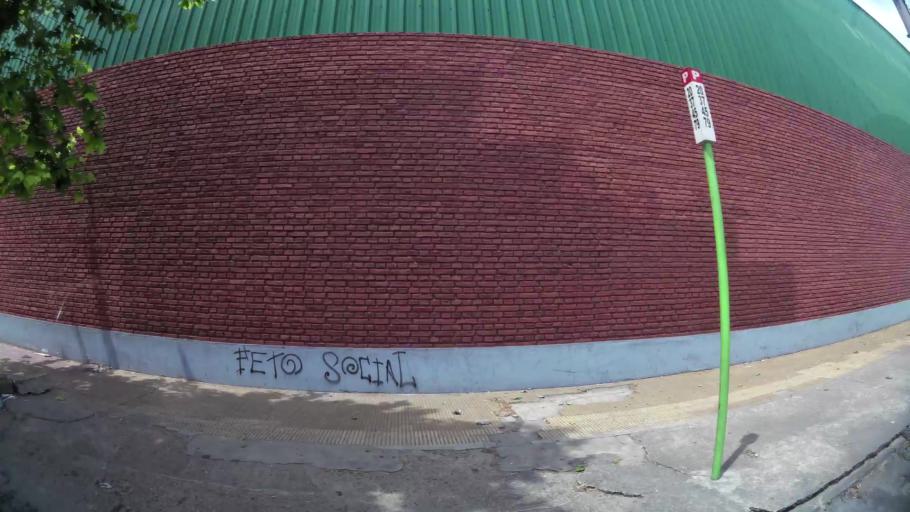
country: AR
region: Buenos Aires
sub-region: Partido de Avellaneda
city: Avellaneda
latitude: -34.6643
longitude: -58.3888
